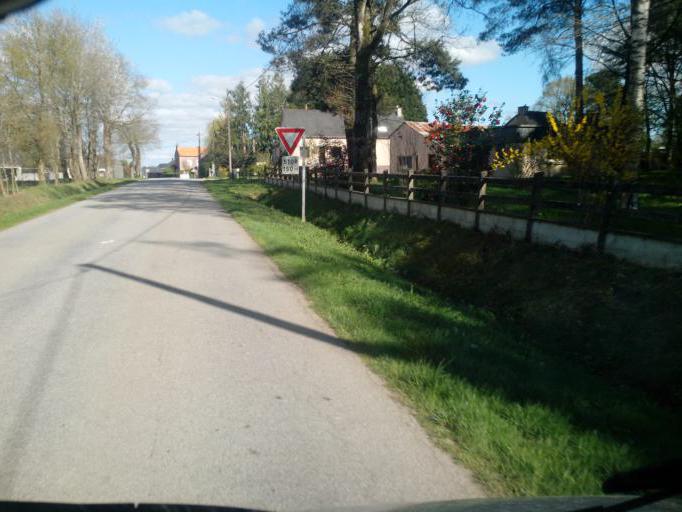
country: FR
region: Brittany
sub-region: Departement d'Ille-et-Vilaine
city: Paimpont
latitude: 48.0660
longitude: -2.1916
